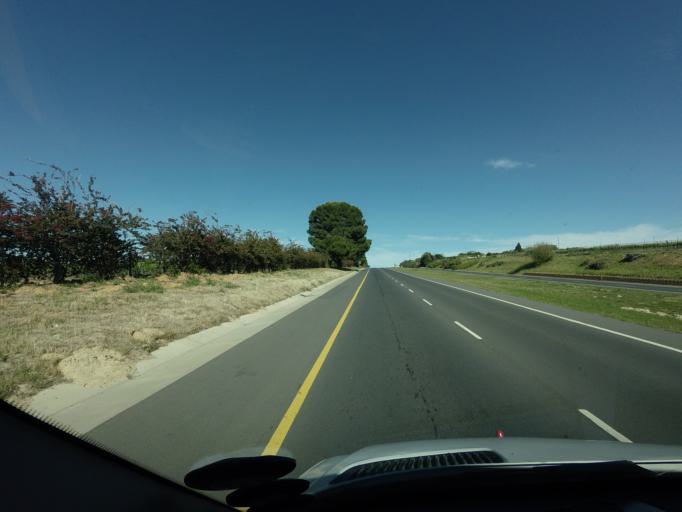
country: ZA
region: Western Cape
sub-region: City of Cape Town
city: Kraaifontein
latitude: -33.9630
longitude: 18.7361
